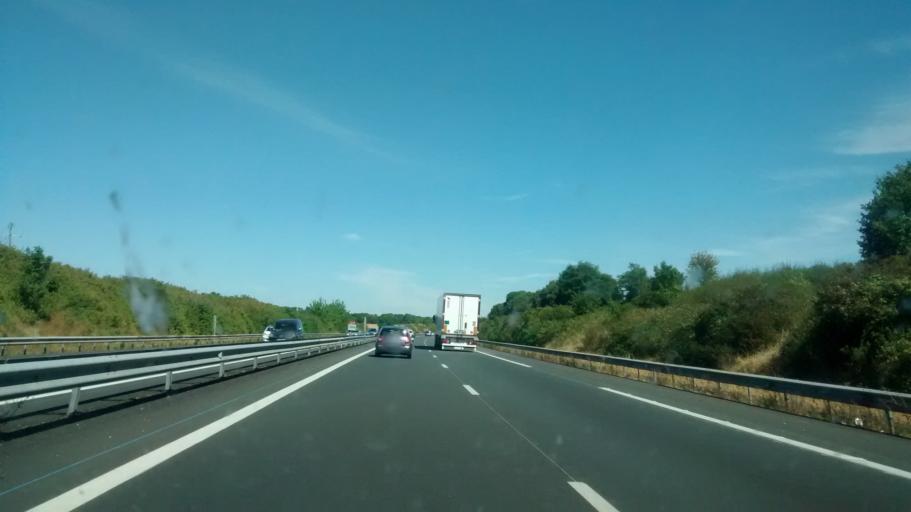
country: FR
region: Poitou-Charentes
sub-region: Departement des Deux-Sevres
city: Vouille
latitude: 46.3204
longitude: -0.3447
